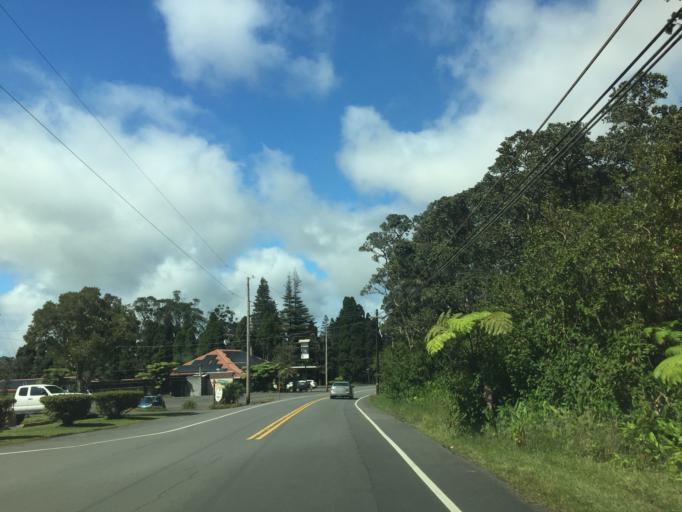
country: US
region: Hawaii
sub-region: Hawaii County
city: Volcano
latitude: 19.4276
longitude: -155.2363
